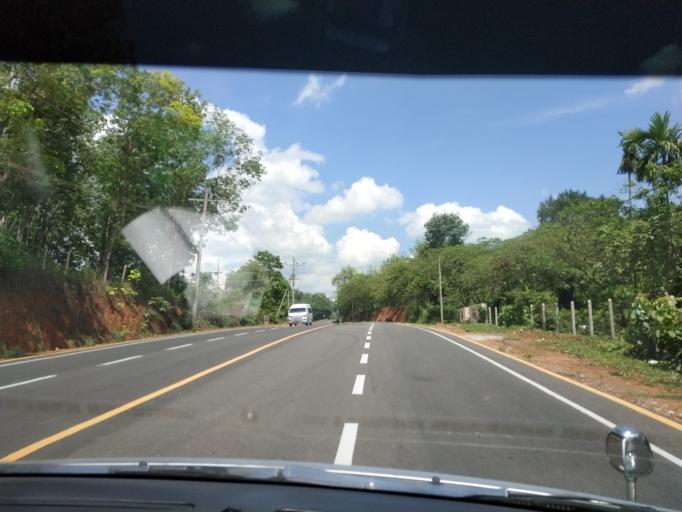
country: MM
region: Mon
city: Kyaikto
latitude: 17.3916
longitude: 97.0642
